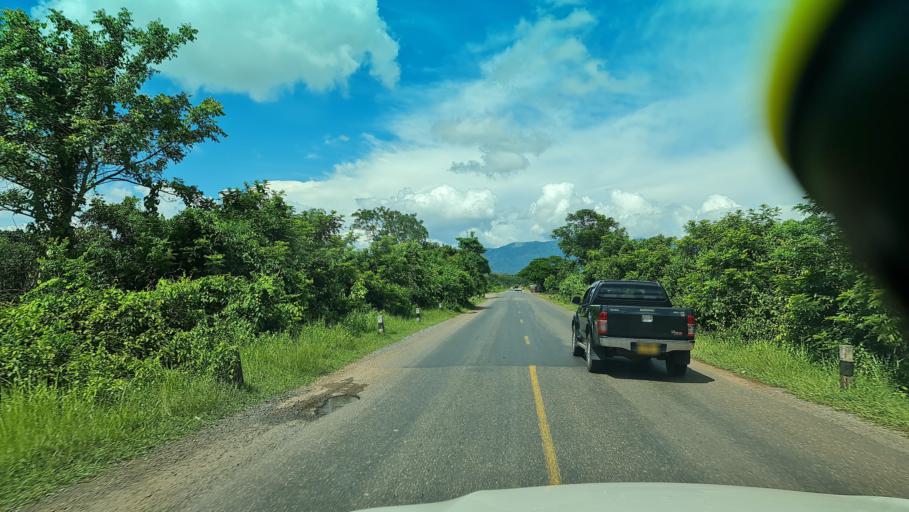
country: LA
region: Bolikhamxai
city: Pakkading
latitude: 18.2799
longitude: 104.0667
